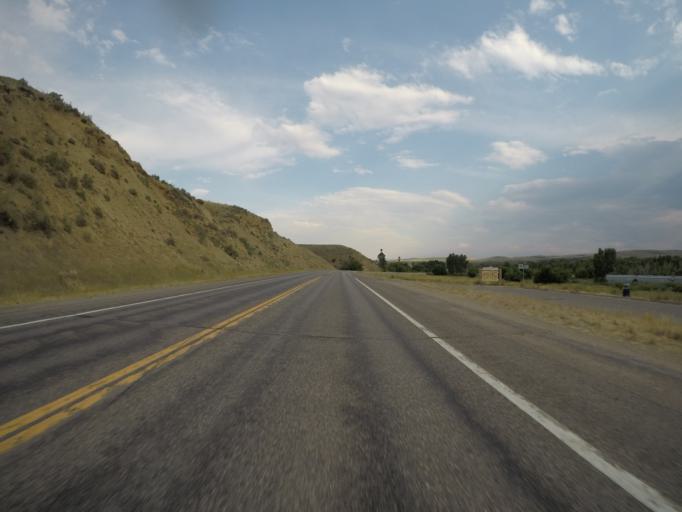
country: US
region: Colorado
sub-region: Routt County
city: Hayden
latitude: 40.5073
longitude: -107.3801
